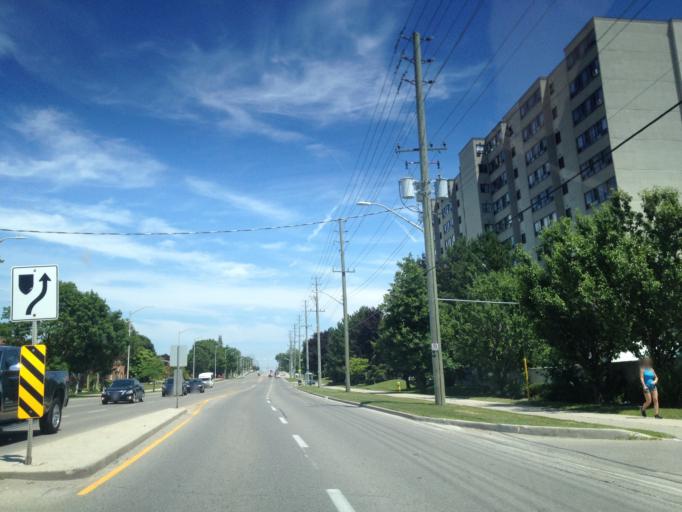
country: CA
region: Ontario
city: London
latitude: 42.9757
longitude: -81.3195
